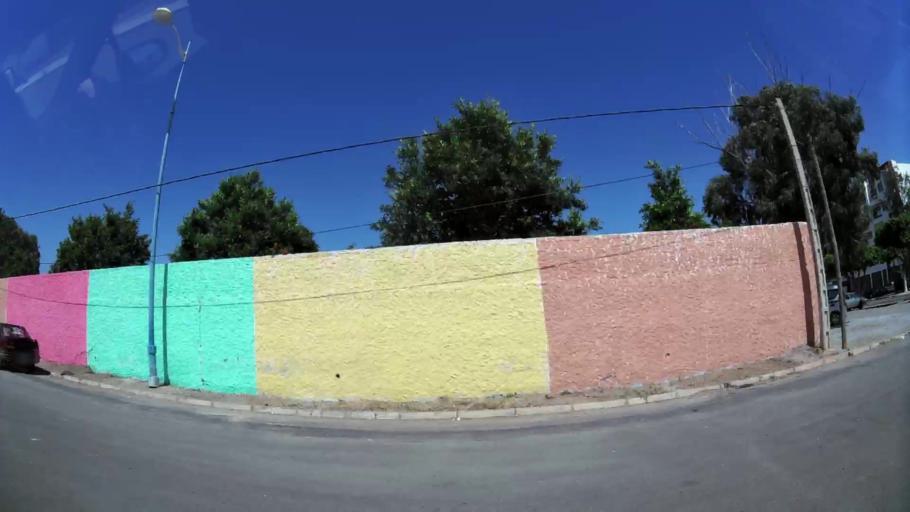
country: MA
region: Souss-Massa-Draa
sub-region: Agadir-Ida-ou-Tnan
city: Agadir
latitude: 30.4098
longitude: -9.5853
